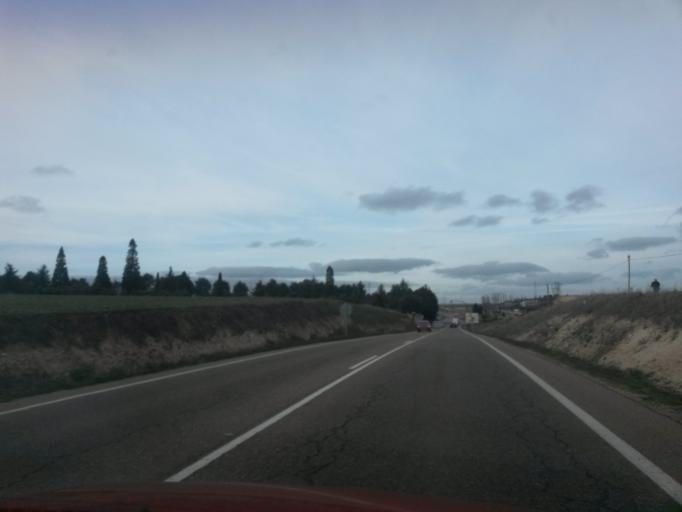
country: ES
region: Castille and Leon
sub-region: Provincia de Salamanca
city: Villares de la Reina
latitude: 40.9909
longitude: -5.6585
